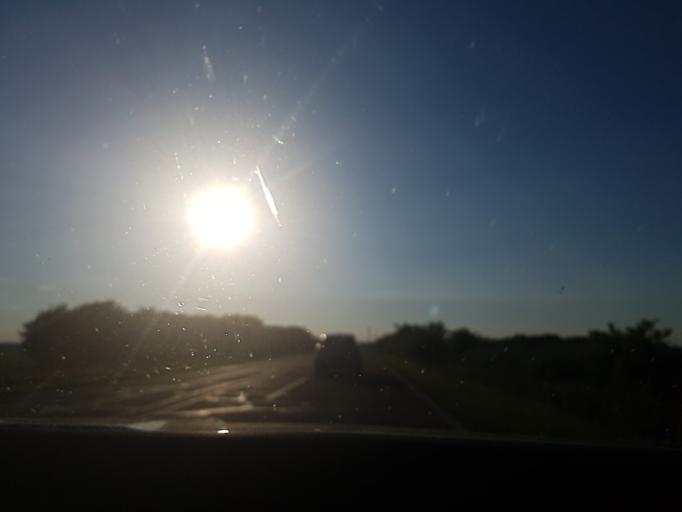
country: RO
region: Timis
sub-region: Comuna Moravita
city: Moravita
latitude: 45.2250
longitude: 21.2899
